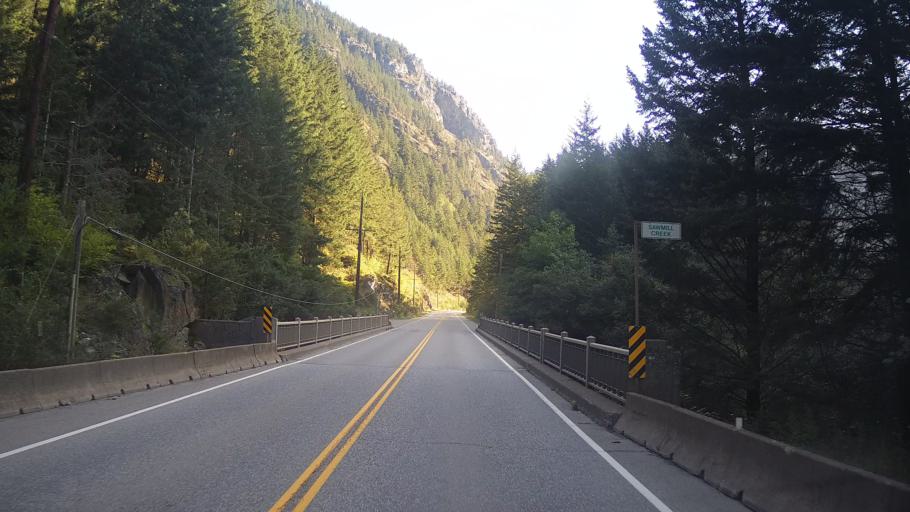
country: CA
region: British Columbia
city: Hope
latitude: 49.6121
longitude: -121.4130
